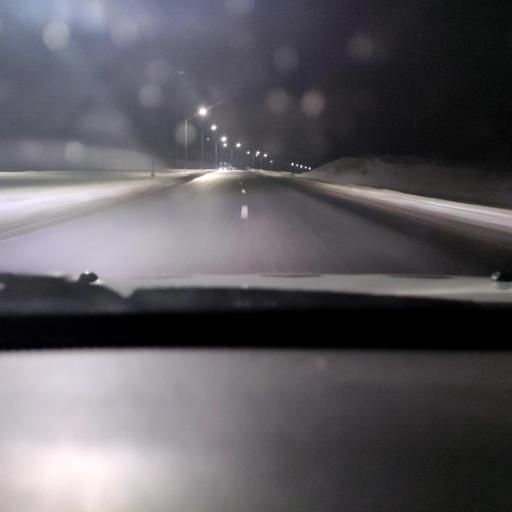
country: RU
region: Perm
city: Novyye Lyady
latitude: 58.0941
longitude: 56.4269
